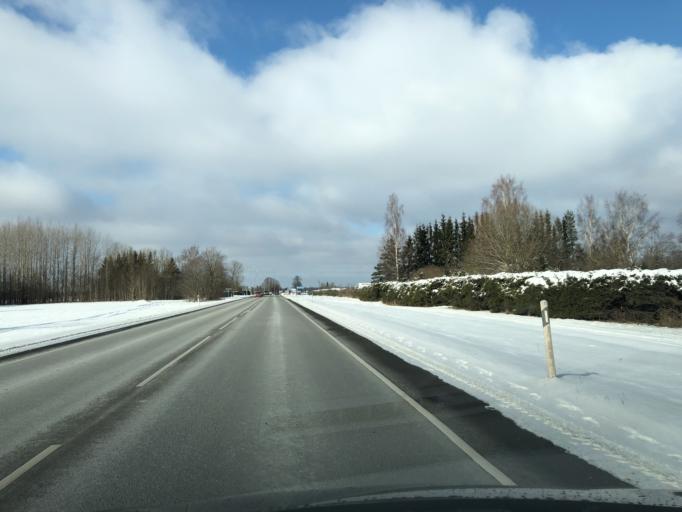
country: EE
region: Jaervamaa
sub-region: Paide linn
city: Paide
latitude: 58.8755
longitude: 25.6973
